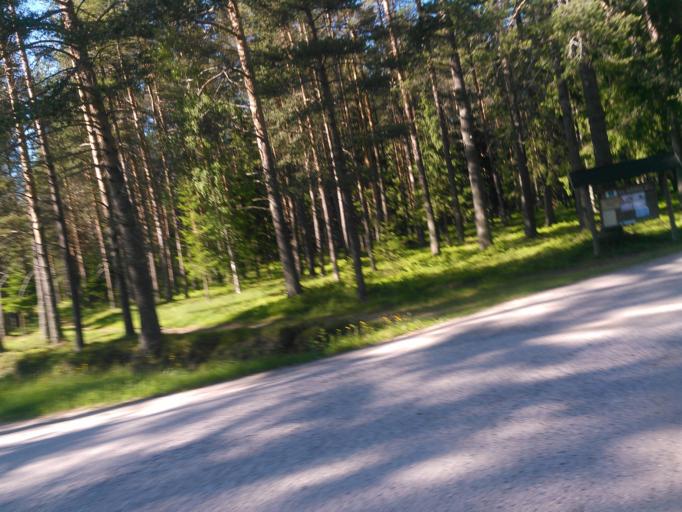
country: SE
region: Vaesterbotten
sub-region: Umea Kommun
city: Roback
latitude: 63.8322
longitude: 20.1092
